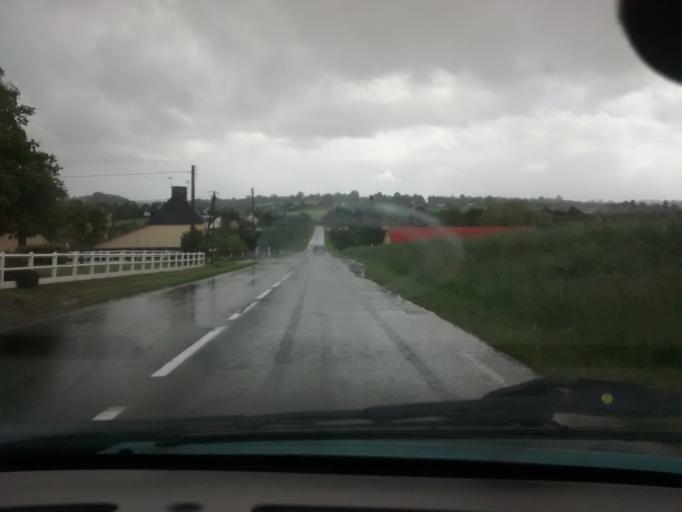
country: FR
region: Lower Normandy
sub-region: Departement de la Manche
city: Conde-sur-Vire
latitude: 49.0625
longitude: -1.0110
